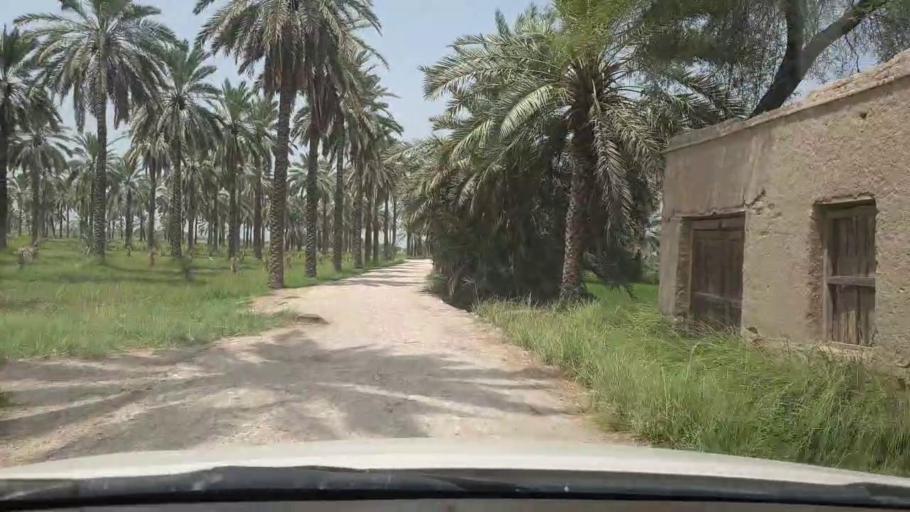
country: PK
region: Sindh
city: Shikarpur
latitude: 28.0179
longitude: 68.6162
